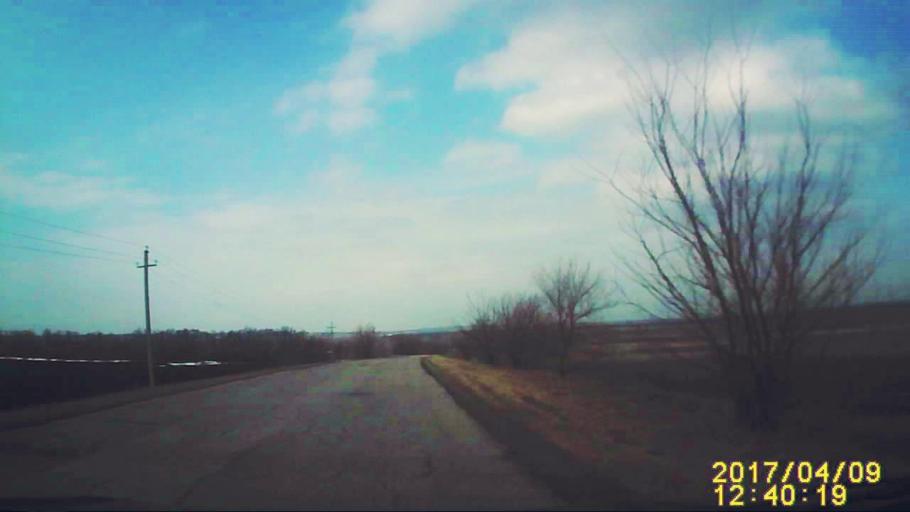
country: RU
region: Ulyanovsk
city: Ignatovka
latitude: 54.0027
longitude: 47.9470
